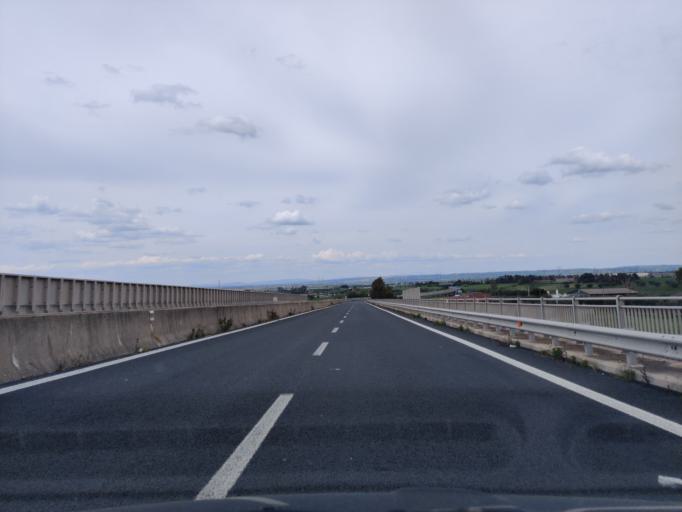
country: IT
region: Latium
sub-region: Citta metropolitana di Roma Capitale
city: Aurelia
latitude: 42.1434
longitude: 11.7927
